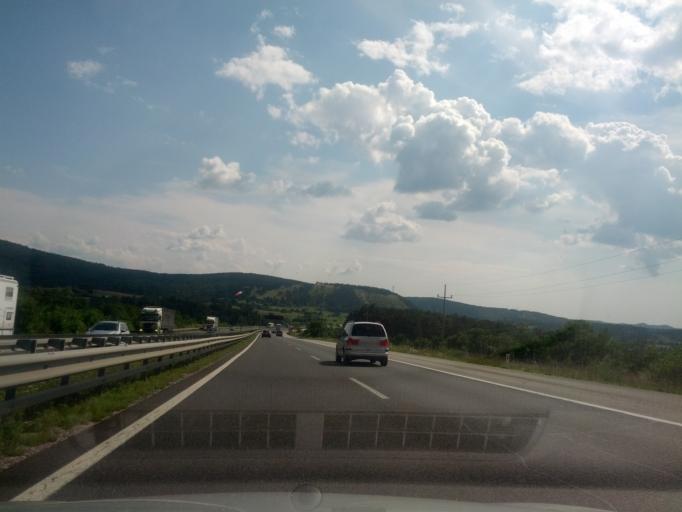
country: SI
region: Divaca
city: Divaca
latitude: 45.7317
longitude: 14.0189
